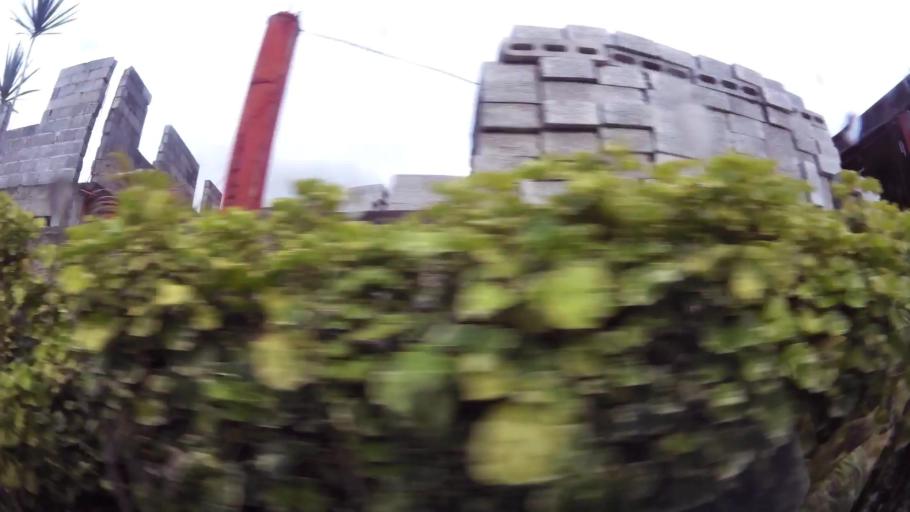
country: DM
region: Saint George
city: Roseau
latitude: 15.3308
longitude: -61.3892
